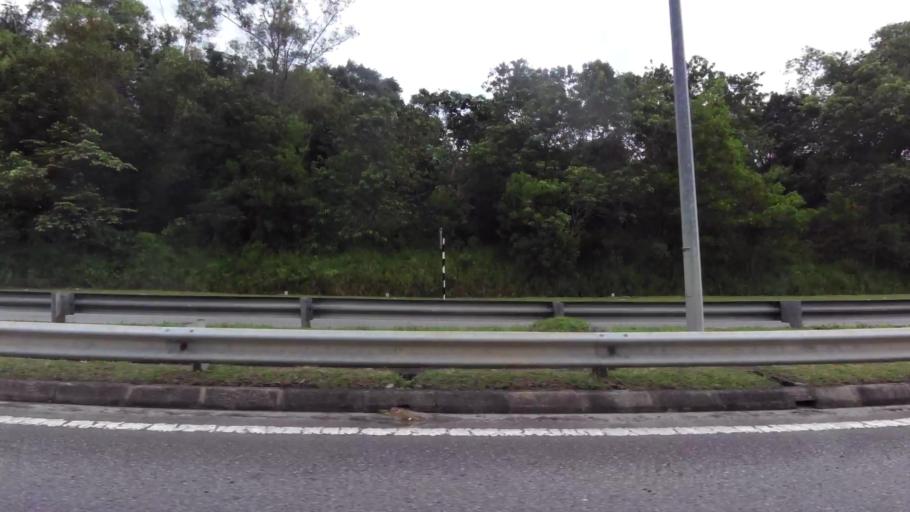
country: BN
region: Brunei and Muara
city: Bandar Seri Begawan
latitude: 4.9106
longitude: 114.9078
